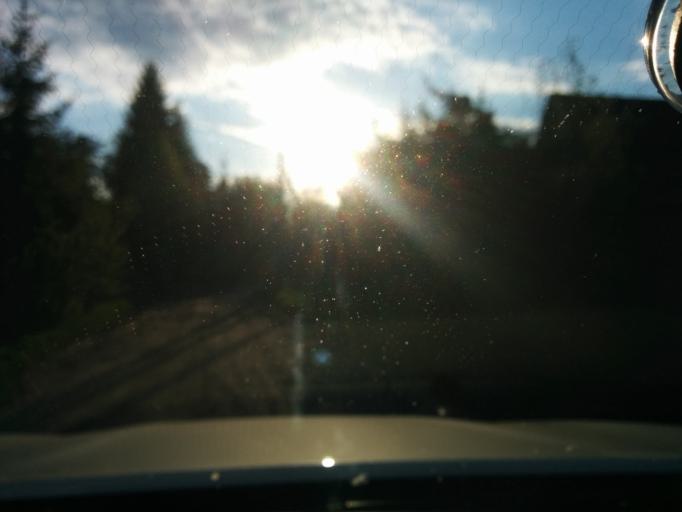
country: RU
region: Leningrad
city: Verkhniye Osel'ki
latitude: 60.2597
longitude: 30.4154
